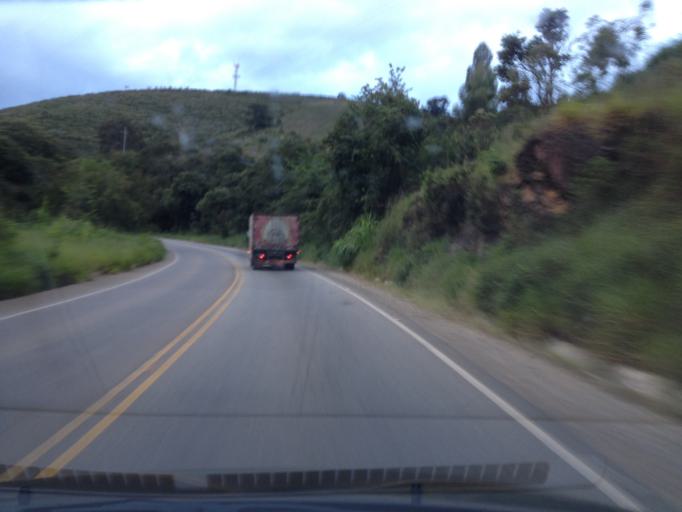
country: BR
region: Minas Gerais
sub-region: Sao Lourenco
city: Sao Lourenco
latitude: -22.0640
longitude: -45.0372
